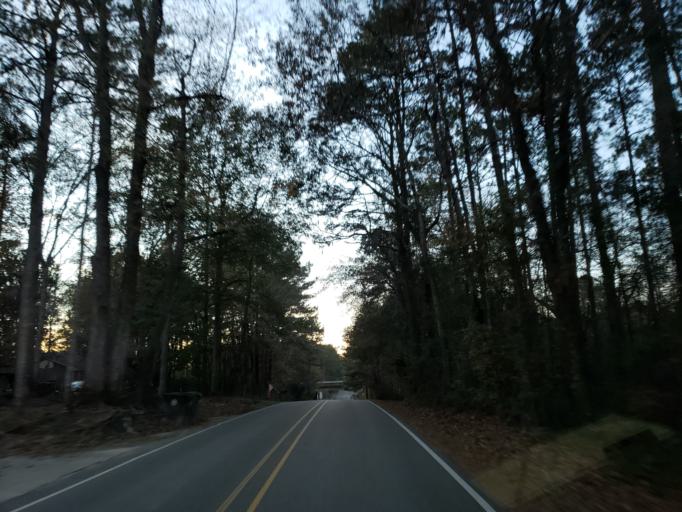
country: US
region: Mississippi
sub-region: Forrest County
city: Hattiesburg
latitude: 31.2445
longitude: -89.3243
